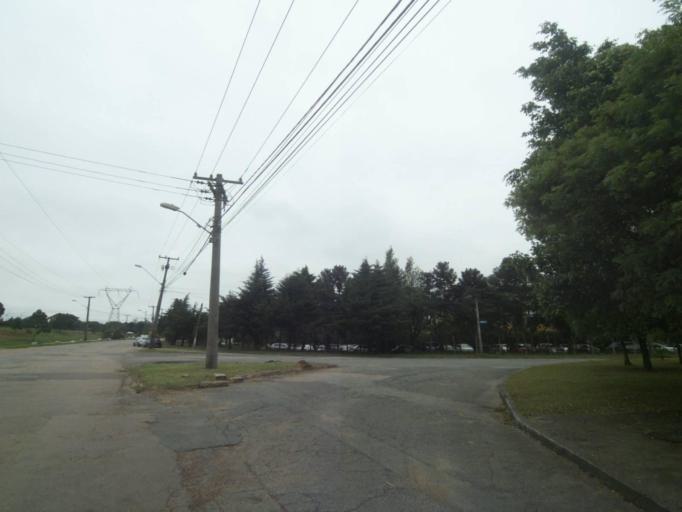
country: BR
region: Parana
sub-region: Araucaria
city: Araucaria
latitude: -25.5447
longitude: -49.3165
